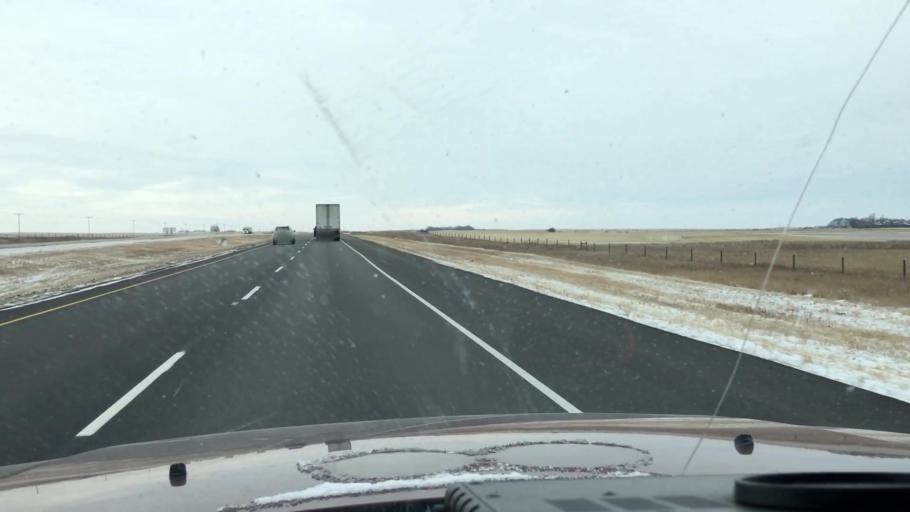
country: CA
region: Saskatchewan
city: Saskatoon
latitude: 51.8011
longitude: -106.4902
